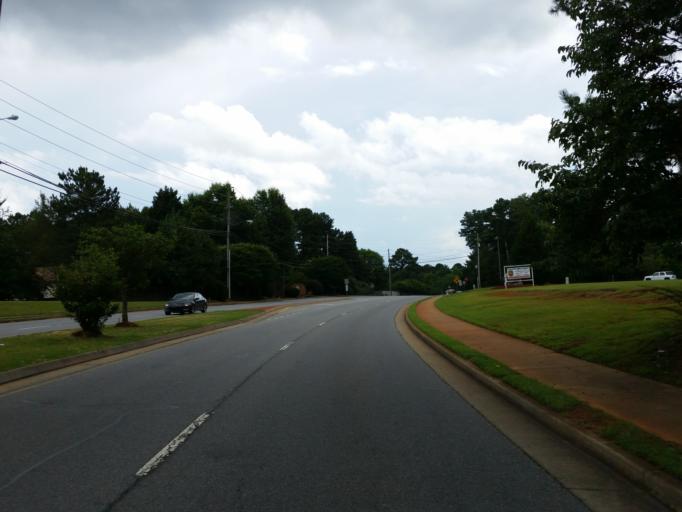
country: US
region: Georgia
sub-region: Cobb County
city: Kennesaw
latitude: 34.0710
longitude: -84.5868
